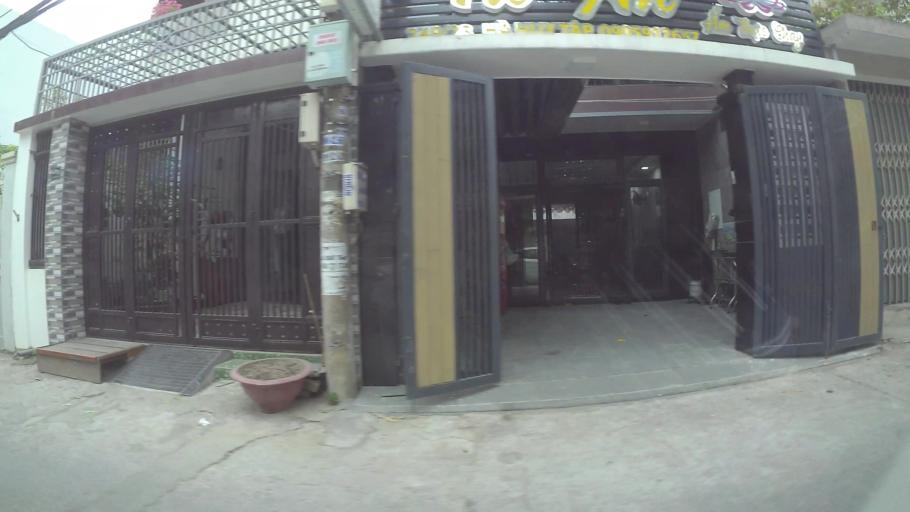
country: VN
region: Da Nang
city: Thanh Khe
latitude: 16.0594
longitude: 108.1888
